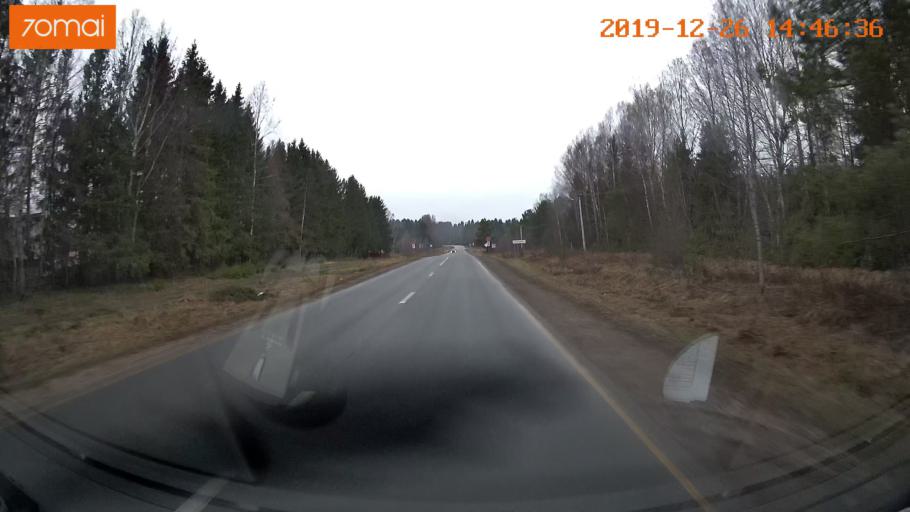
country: RU
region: Jaroslavl
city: Poshekhon'ye
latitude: 58.3376
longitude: 39.0147
